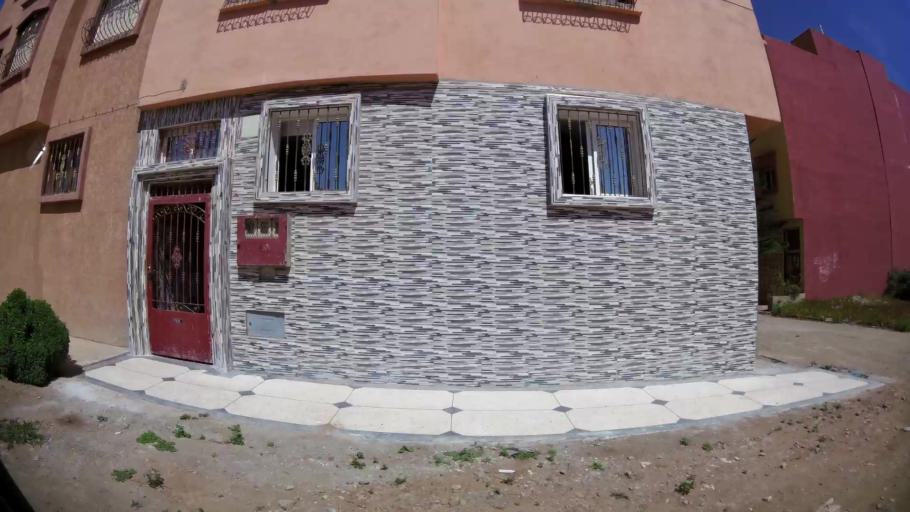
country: MA
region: Souss-Massa-Draa
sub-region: Inezgane-Ait Mellou
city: Inezgane
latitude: 30.3286
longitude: -9.5082
